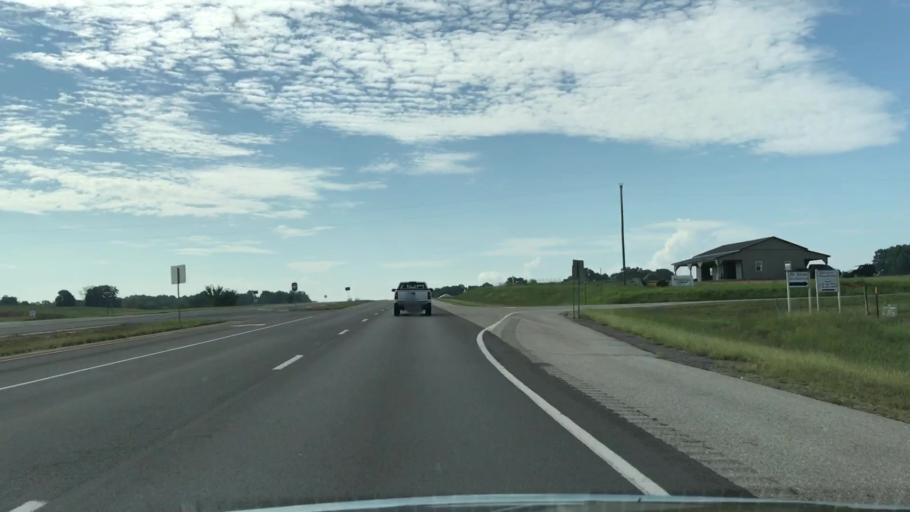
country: US
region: Kentucky
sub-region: Warren County
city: Plano
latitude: 36.8247
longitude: -86.3109
